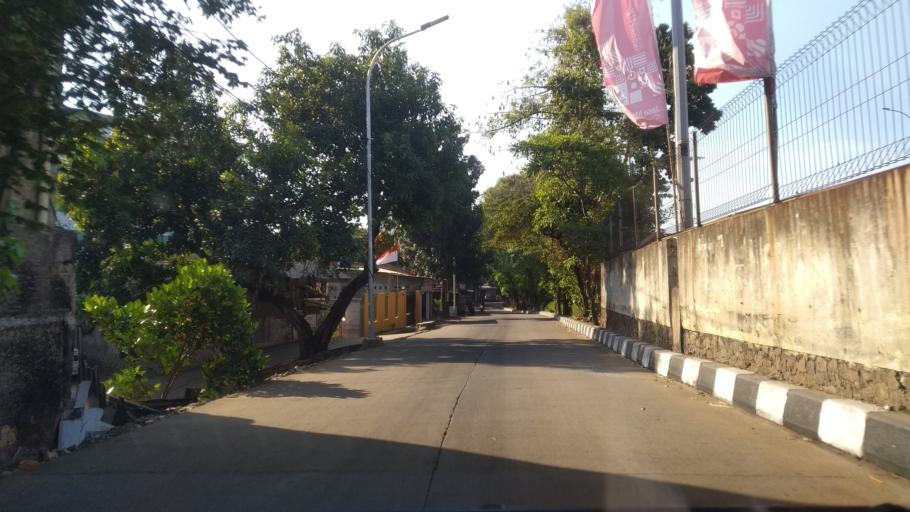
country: ID
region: Banten
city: South Tangerang
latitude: -6.2595
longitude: 106.7657
